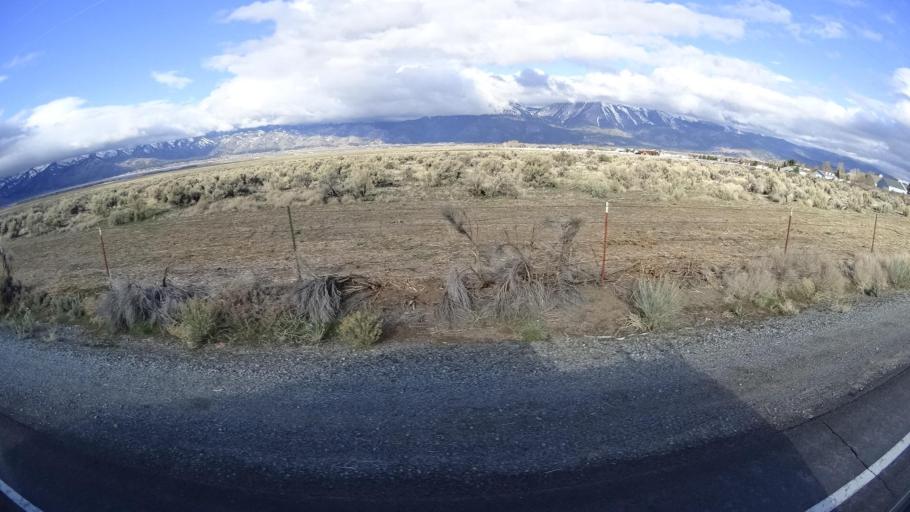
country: US
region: Nevada
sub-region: Carson City
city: Carson City
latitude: 39.2720
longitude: -119.7565
